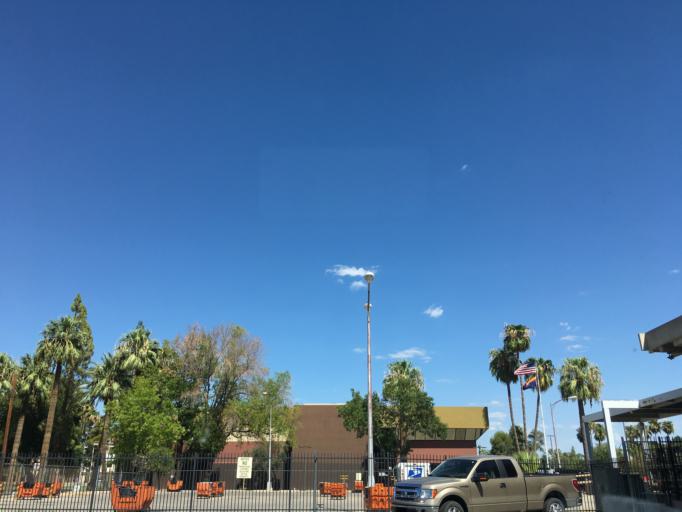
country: US
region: Arizona
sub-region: Maricopa County
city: Mesa
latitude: 33.4182
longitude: -111.8308
